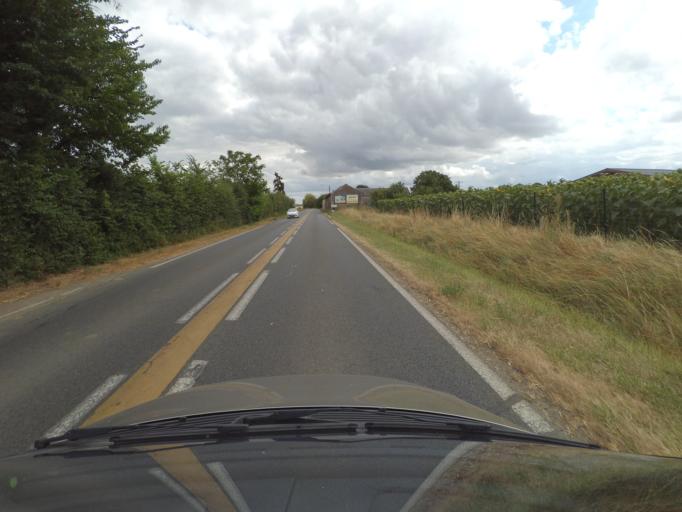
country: FR
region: Centre
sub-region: Departement d'Indre-et-Loire
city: Richelieu
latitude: 47.0079
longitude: 0.2683
